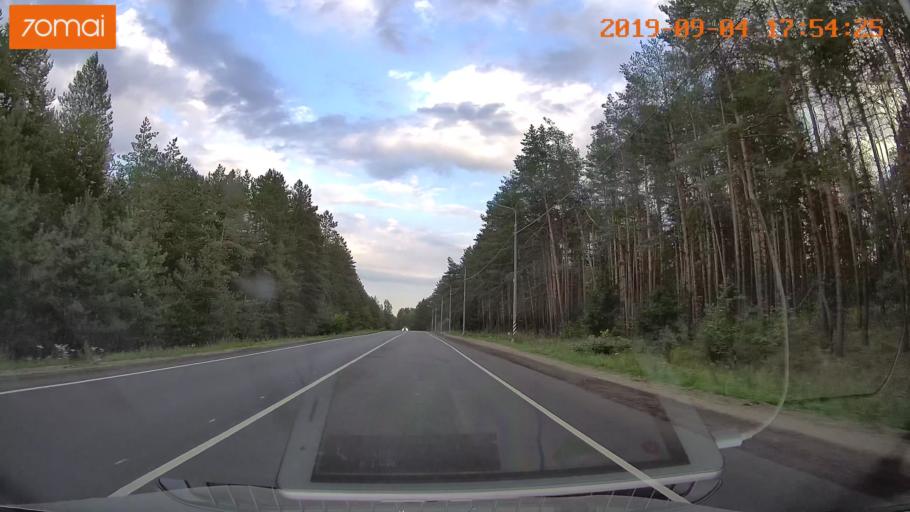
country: RU
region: Moskovskaya
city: Imeni Tsyurupy
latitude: 55.5107
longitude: 38.7444
